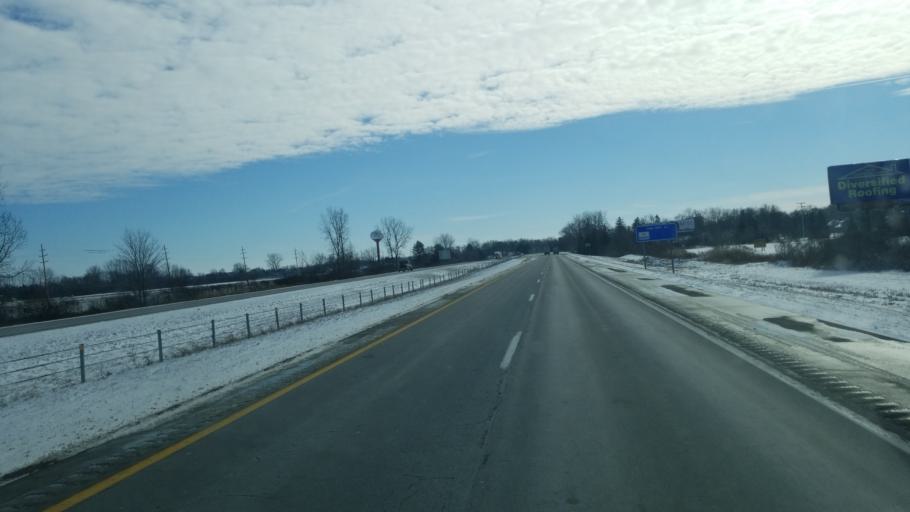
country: US
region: Michigan
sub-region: Washtenaw County
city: Milan
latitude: 42.0939
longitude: -83.6749
